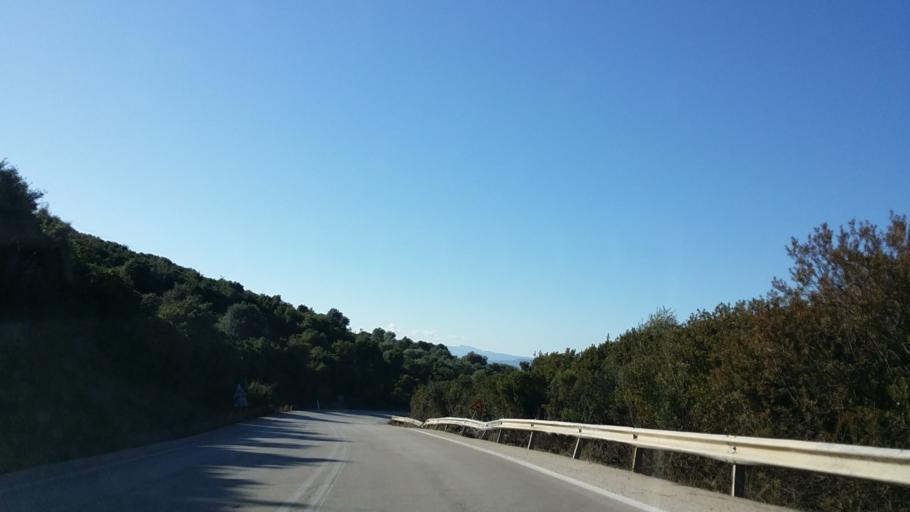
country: GR
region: West Greece
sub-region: Nomos Aitolias kai Akarnanias
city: Vonitsa
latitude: 38.9287
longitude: 20.9161
